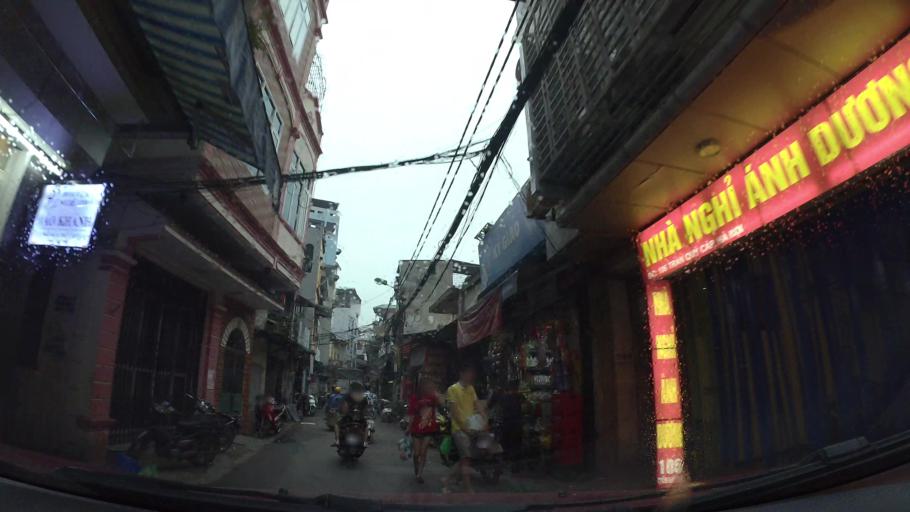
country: VN
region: Ha Noi
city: Hanoi
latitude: 21.0225
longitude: 105.8391
